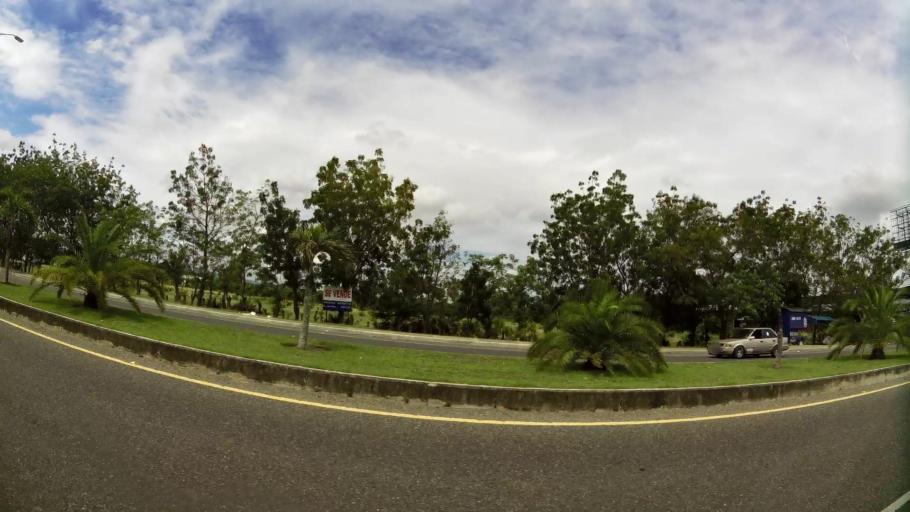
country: DO
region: Santiago
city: Licey al Medio
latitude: 19.3986
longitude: -70.6029
